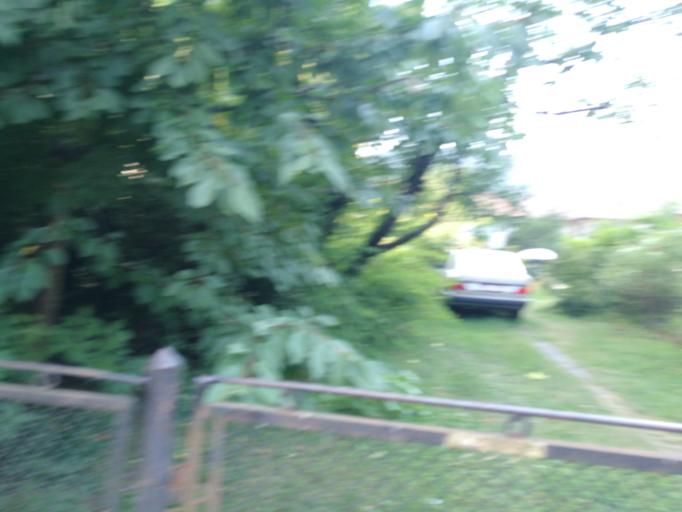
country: RO
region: Neamt
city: Piatra Neamt
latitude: 46.9337
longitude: 26.3641
